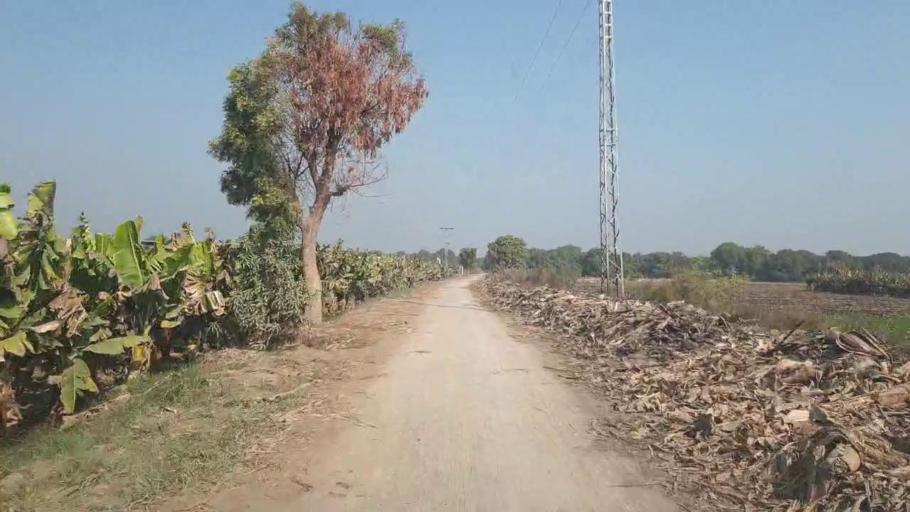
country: PK
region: Sindh
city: Tando Allahyar
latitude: 25.4675
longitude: 68.7839
